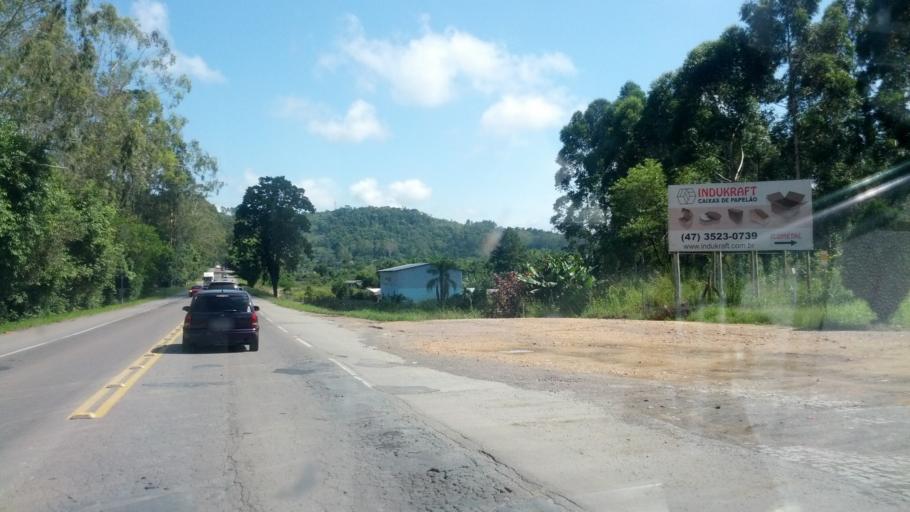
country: BR
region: Santa Catarina
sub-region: Rio Do Sul
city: Rio do Sul
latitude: -27.1584
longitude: -49.5565
